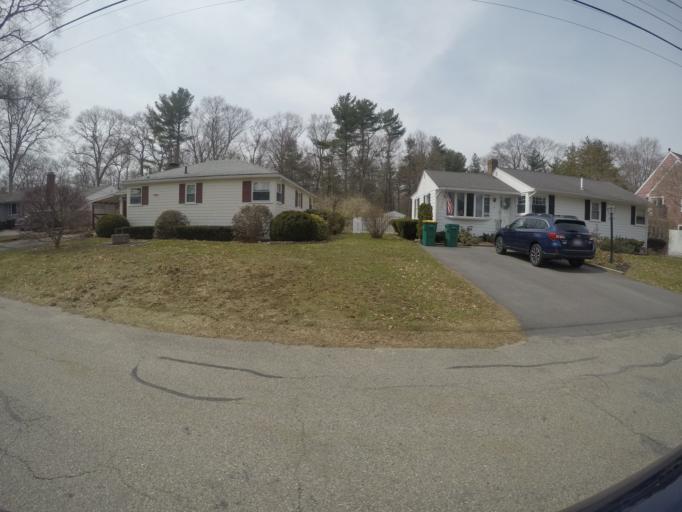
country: US
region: Massachusetts
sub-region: Bristol County
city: Easton
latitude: 42.0614
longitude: -71.1107
